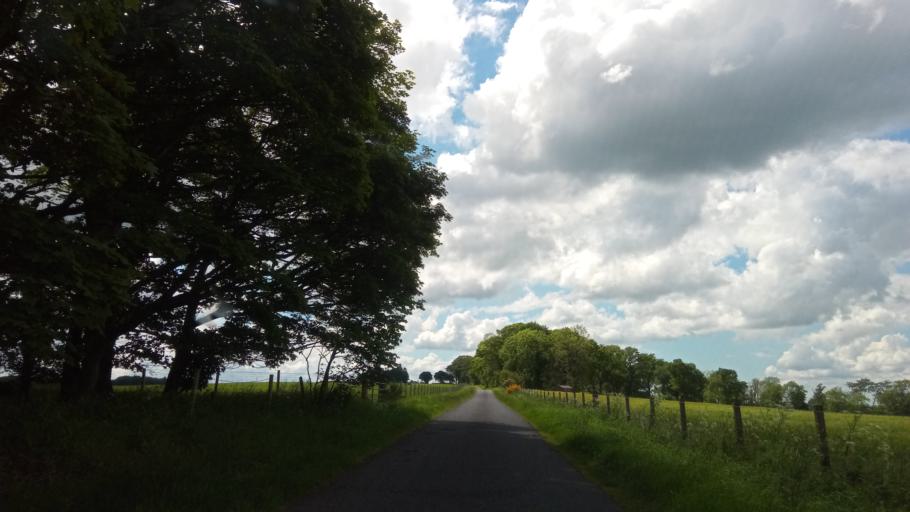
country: GB
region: Scotland
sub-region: The Scottish Borders
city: Coldstream
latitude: 55.5914
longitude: -2.2903
